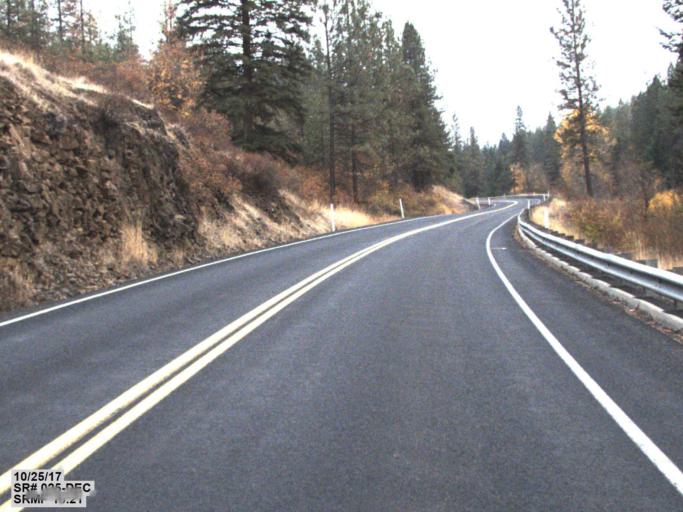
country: US
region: Washington
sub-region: Lincoln County
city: Davenport
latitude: 47.8704
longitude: -118.2646
